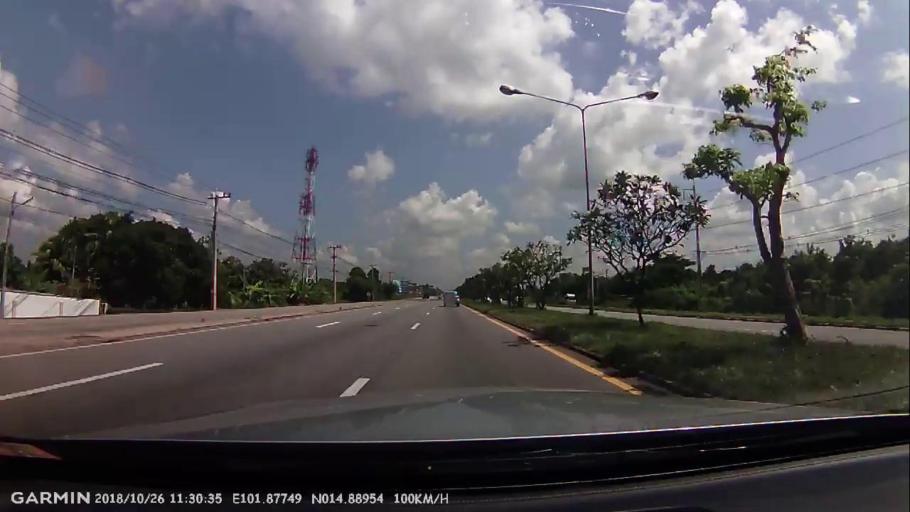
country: TH
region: Nakhon Ratchasima
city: Sung Noen
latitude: 14.8897
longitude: 101.8776
